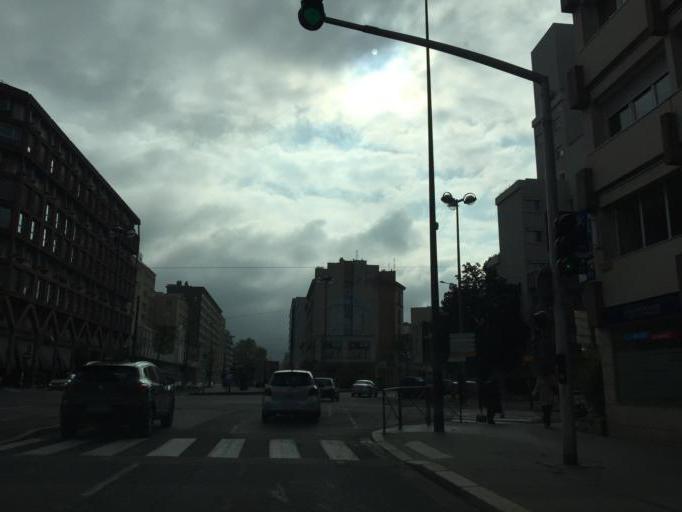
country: FR
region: Rhone-Alpes
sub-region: Departement de la Loire
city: Saint-Etienne
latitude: 45.4543
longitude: 4.3829
